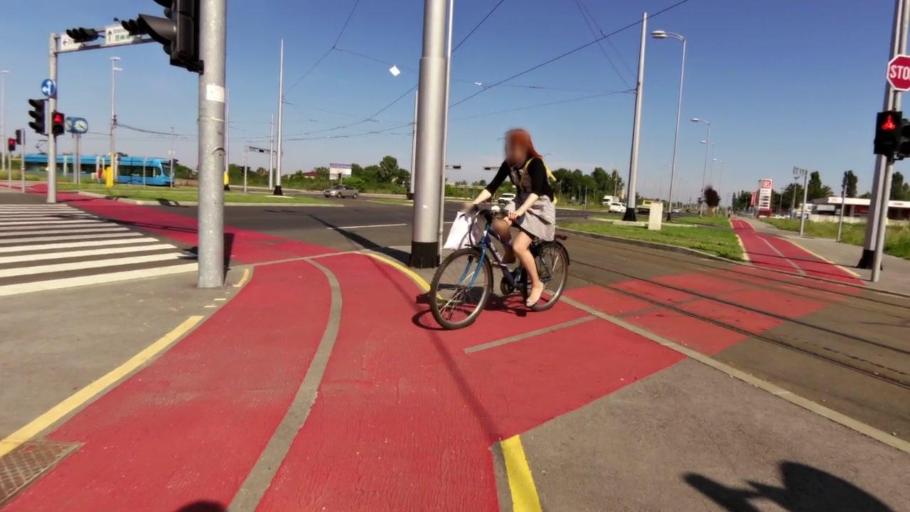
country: HR
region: Zagrebacka
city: Micevec
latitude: 45.7890
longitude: 16.0341
